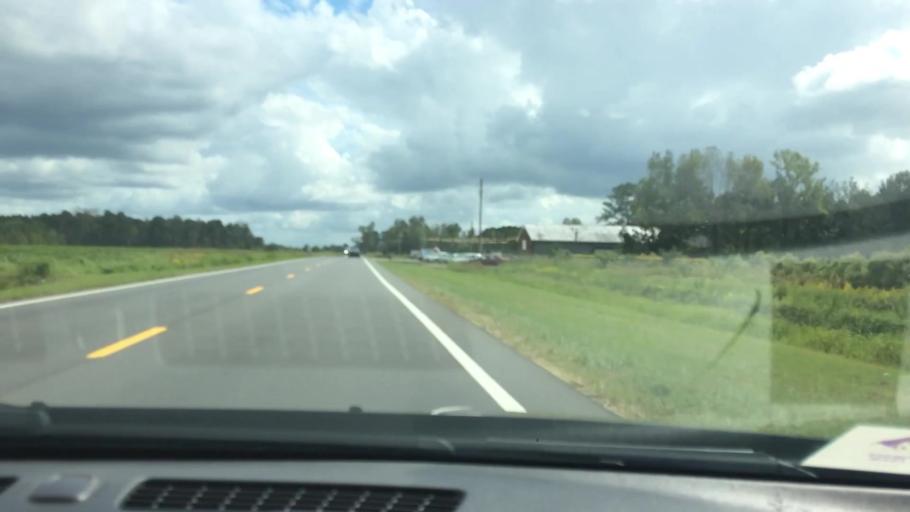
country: US
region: North Carolina
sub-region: Pitt County
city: Farmville
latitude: 35.5599
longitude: -77.5599
